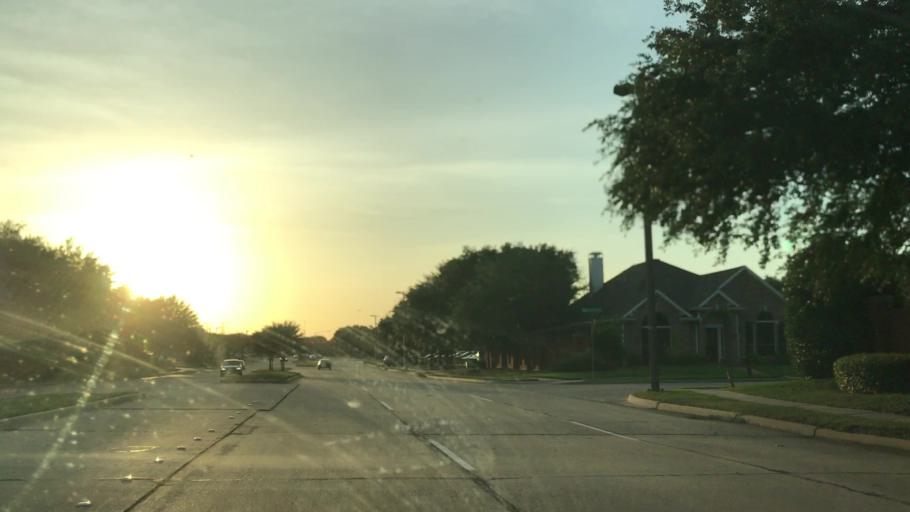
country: US
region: Texas
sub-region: Dallas County
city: Farmers Branch
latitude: 32.9222
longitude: -96.9529
